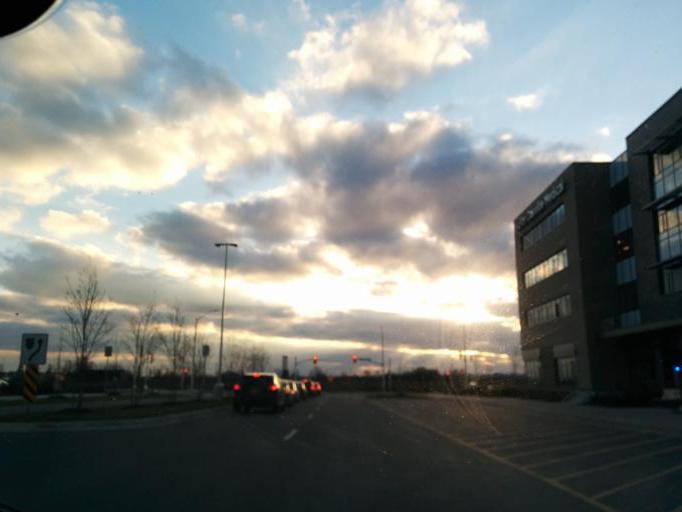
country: CA
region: Ontario
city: Oakville
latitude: 43.4497
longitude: -79.7661
